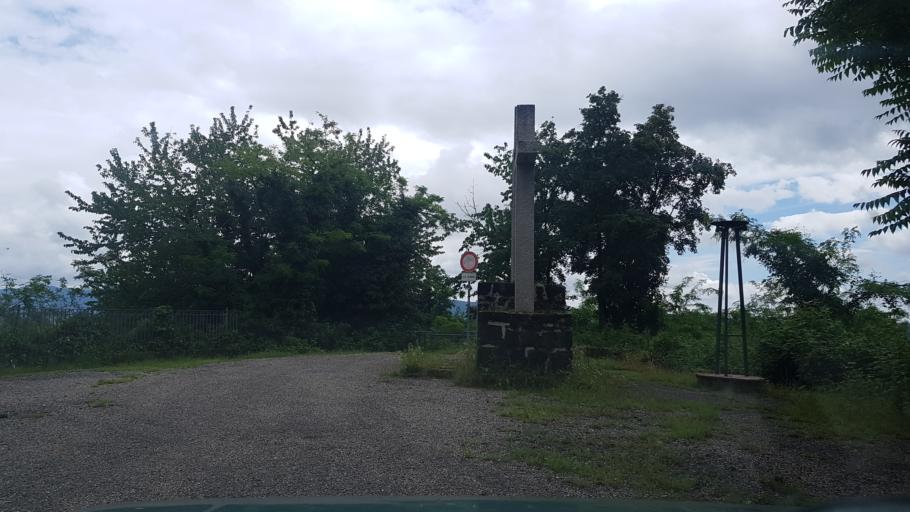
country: IT
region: Friuli Venezia Giulia
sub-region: Provincia di Gorizia
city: Gorizia
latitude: 45.9433
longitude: 13.5904
